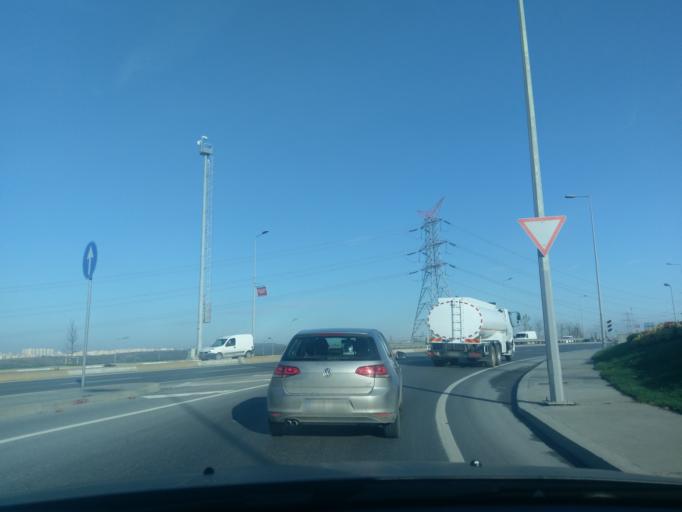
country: TR
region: Istanbul
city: Mahmutbey
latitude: 41.0682
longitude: 28.8336
